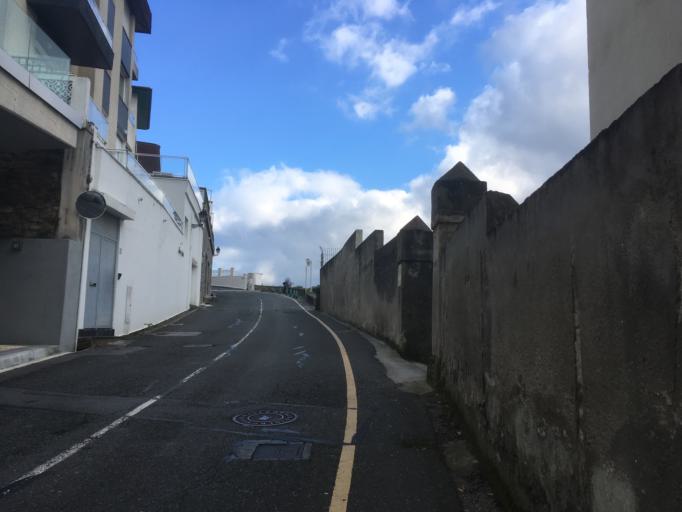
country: ES
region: Basque Country
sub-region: Provincia de Guipuzcoa
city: San Sebastian
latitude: 43.3194
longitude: -2.0061
